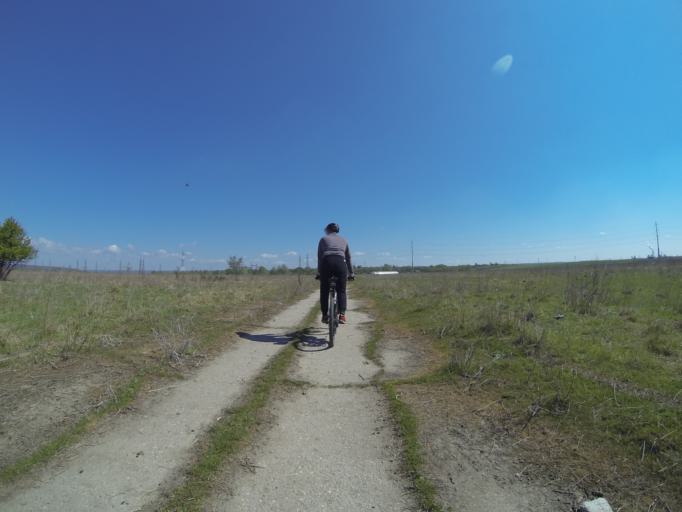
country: RO
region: Dolj
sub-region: Comuna Isalnita
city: Isalnita
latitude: 44.3710
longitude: 23.7486
